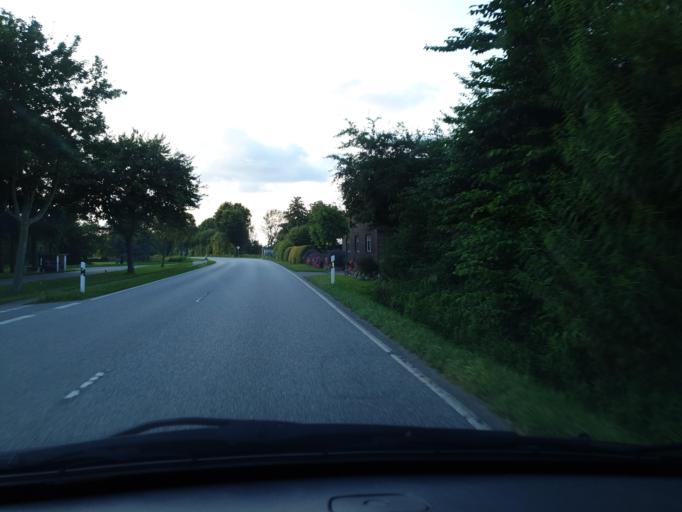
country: DE
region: Schleswig-Holstein
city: Diekhusen-Fahrstedt
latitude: 53.9319
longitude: 9.0343
